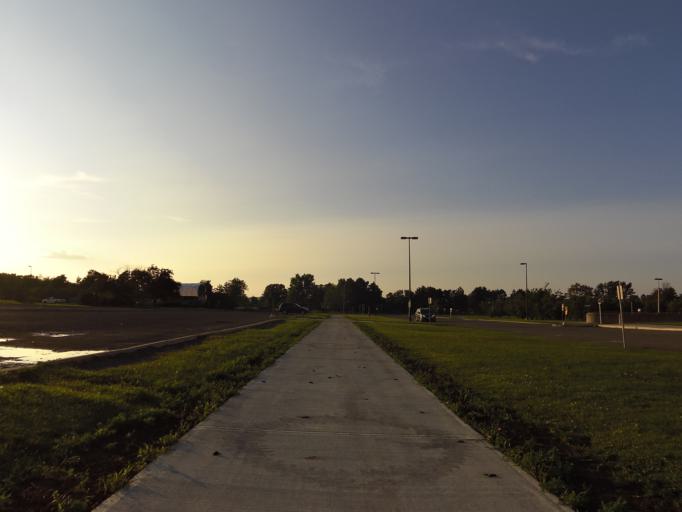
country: CA
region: Ontario
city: Ottawa
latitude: 45.4059
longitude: -75.7397
